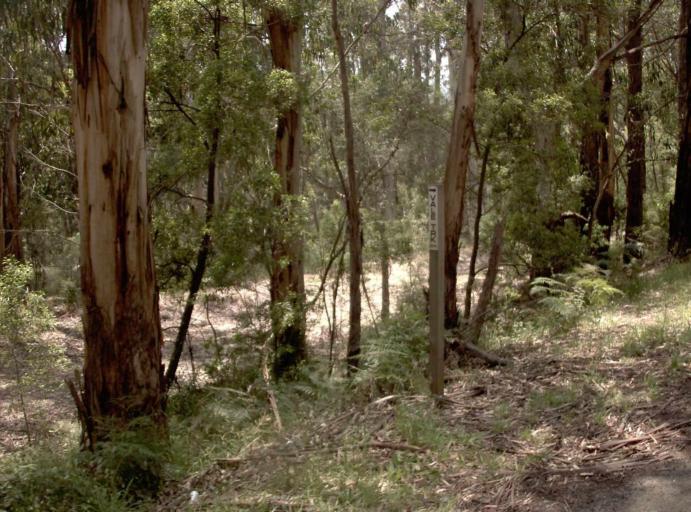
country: AU
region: Victoria
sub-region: Latrobe
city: Traralgon
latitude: -38.3587
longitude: 146.7470
